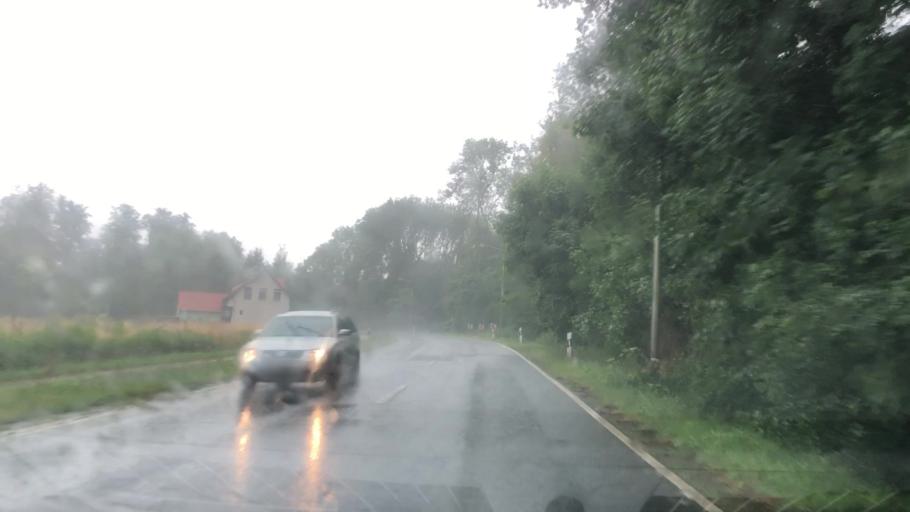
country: DE
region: Lower Saxony
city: Buckeburg
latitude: 52.2668
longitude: 8.9813
